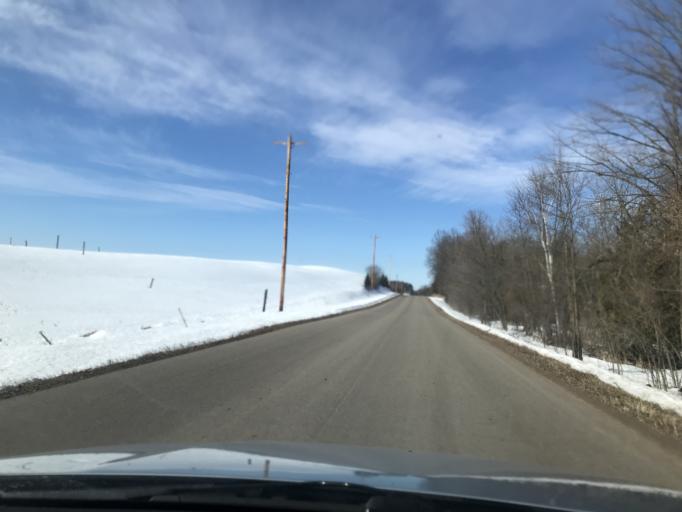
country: US
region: Wisconsin
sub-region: Oconto County
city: Gillett
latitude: 44.9617
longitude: -88.2874
